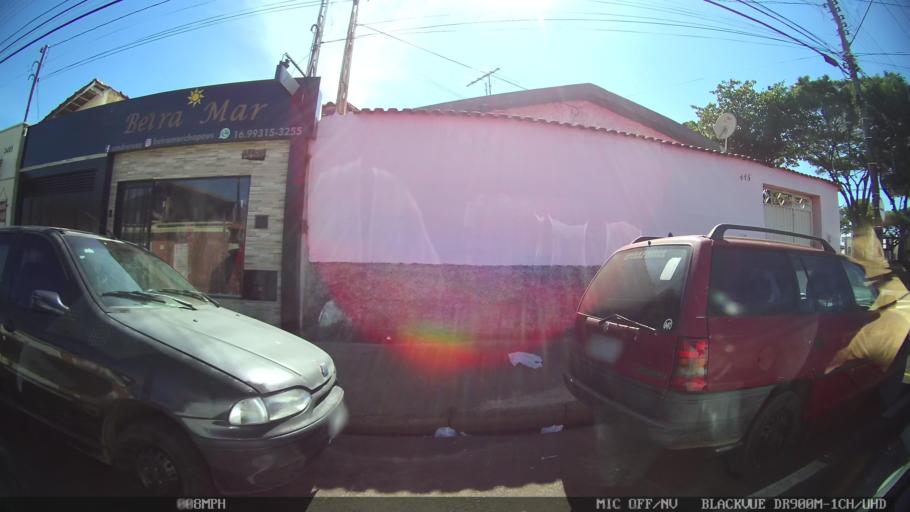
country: BR
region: Sao Paulo
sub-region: Franca
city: Franca
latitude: -20.5469
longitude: -47.3850
